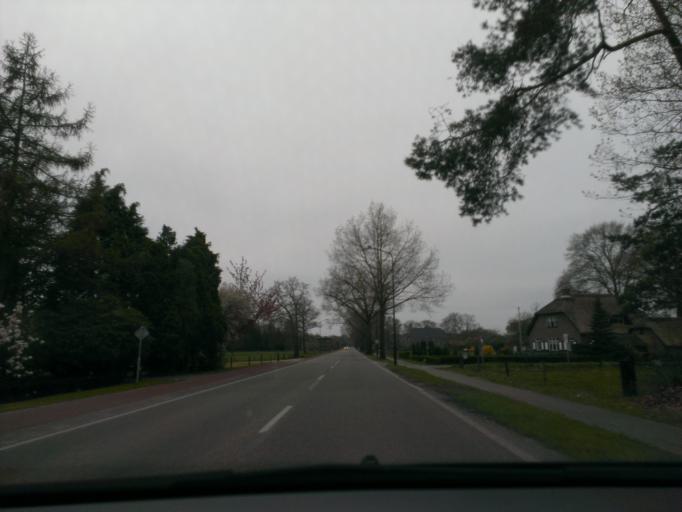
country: NL
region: Gelderland
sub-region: Gemeente Epe
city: Vaassen
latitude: 52.2681
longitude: 5.9573
